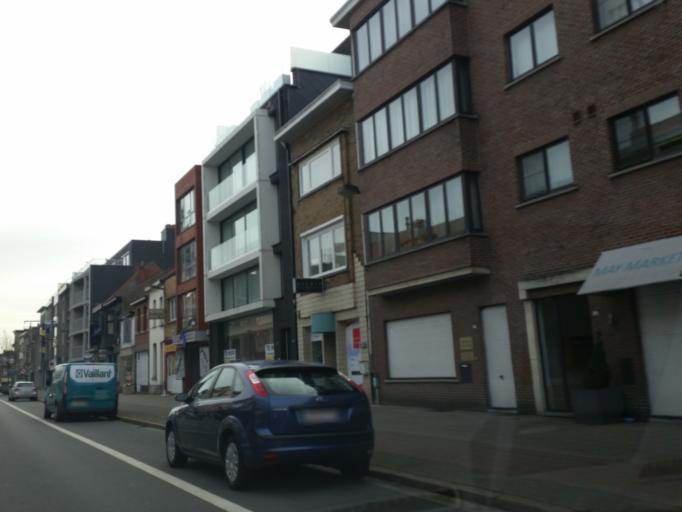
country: BE
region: Flanders
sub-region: Provincie Antwerpen
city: Brasschaat
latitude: 51.2864
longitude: 4.4853
